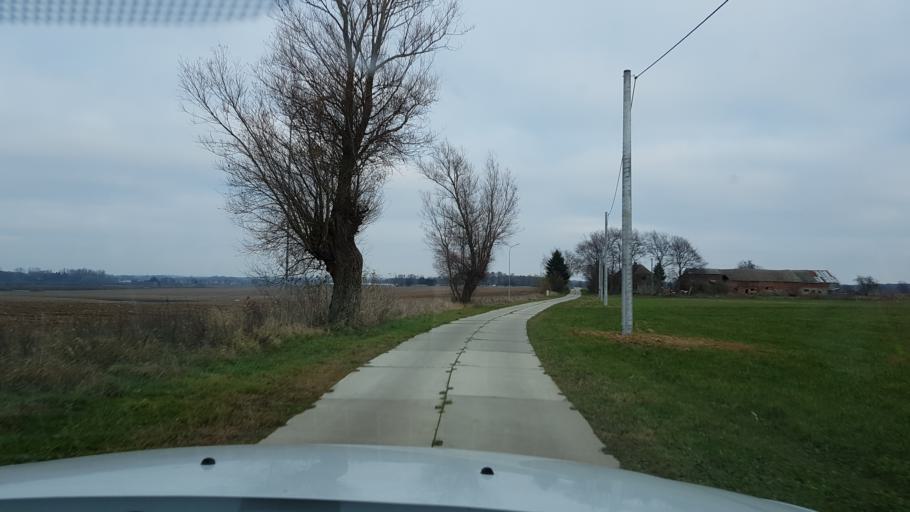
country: PL
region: West Pomeranian Voivodeship
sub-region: Powiat kolobrzeski
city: Kolobrzeg
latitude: 54.1213
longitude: 15.5432
